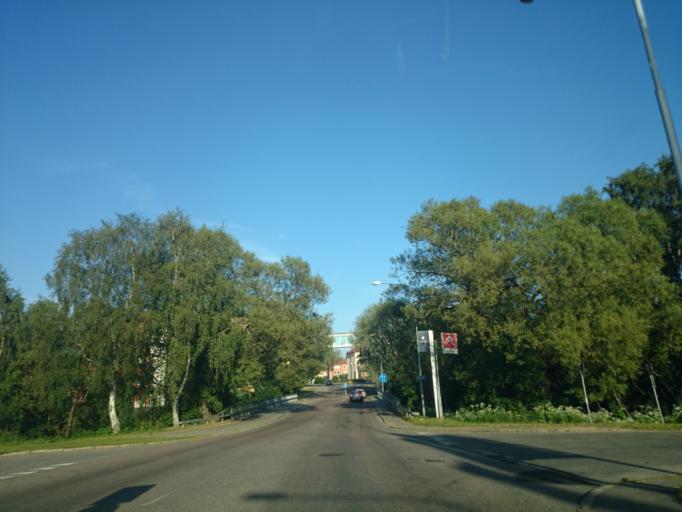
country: SE
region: Vaesternorrland
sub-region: Sundsvalls Kommun
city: Sundsvall
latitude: 62.3937
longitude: 17.2797
